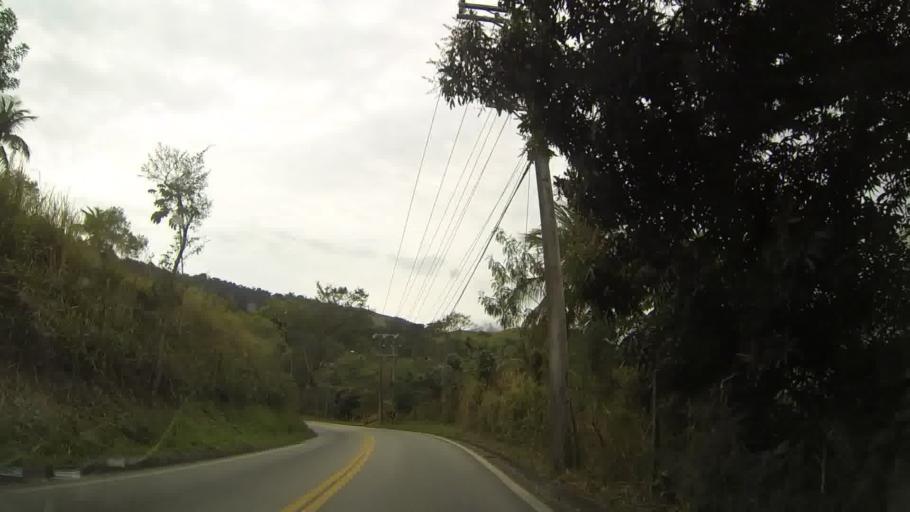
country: BR
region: Sao Paulo
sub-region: Sao Sebastiao
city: Sao Sebastiao
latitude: -23.8234
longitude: -45.4215
